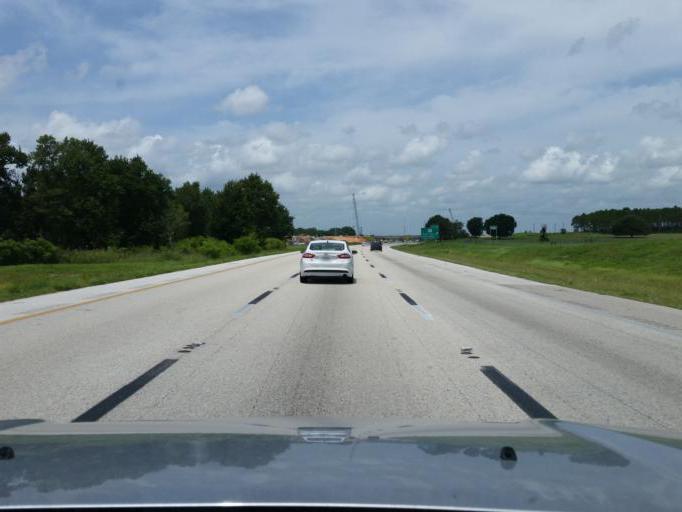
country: US
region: Florida
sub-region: Polk County
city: Polk City
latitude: 28.1583
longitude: -81.7934
